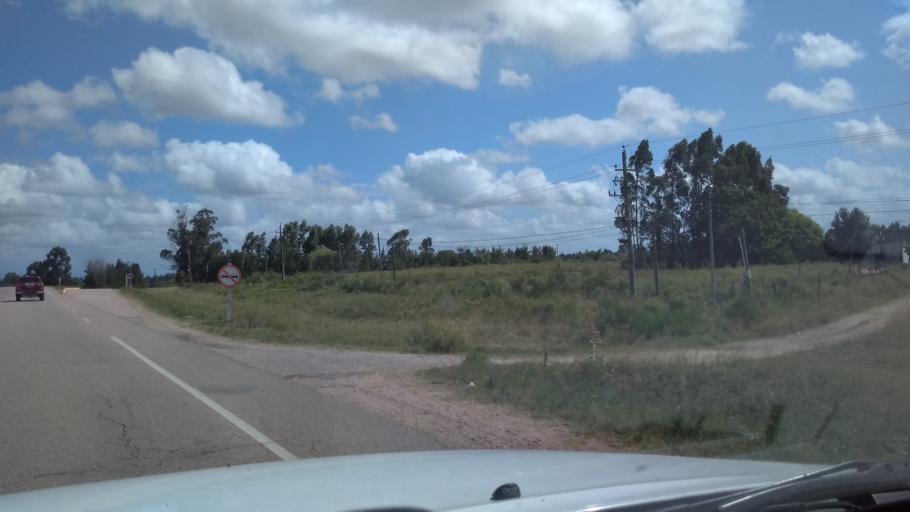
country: UY
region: Canelones
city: Sauce
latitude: -34.6367
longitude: -56.0525
